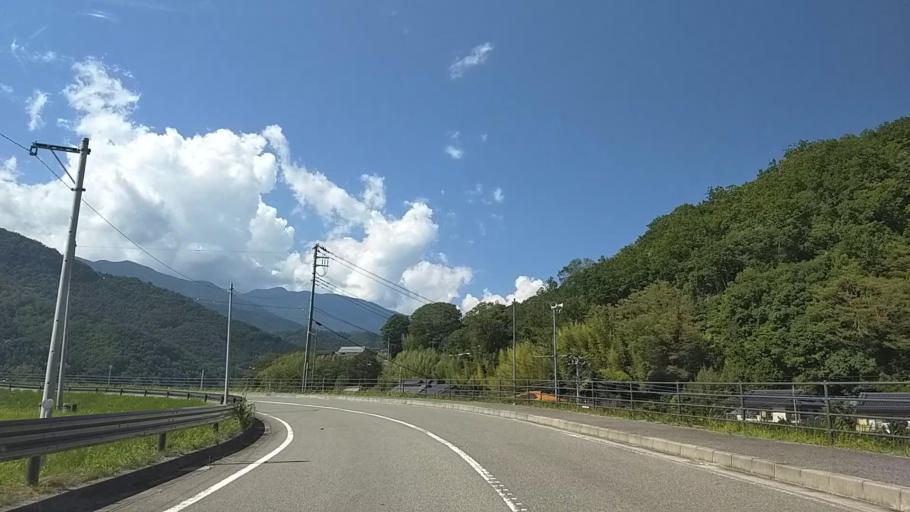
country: JP
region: Yamanashi
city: Ryuo
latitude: 35.5127
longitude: 138.4605
